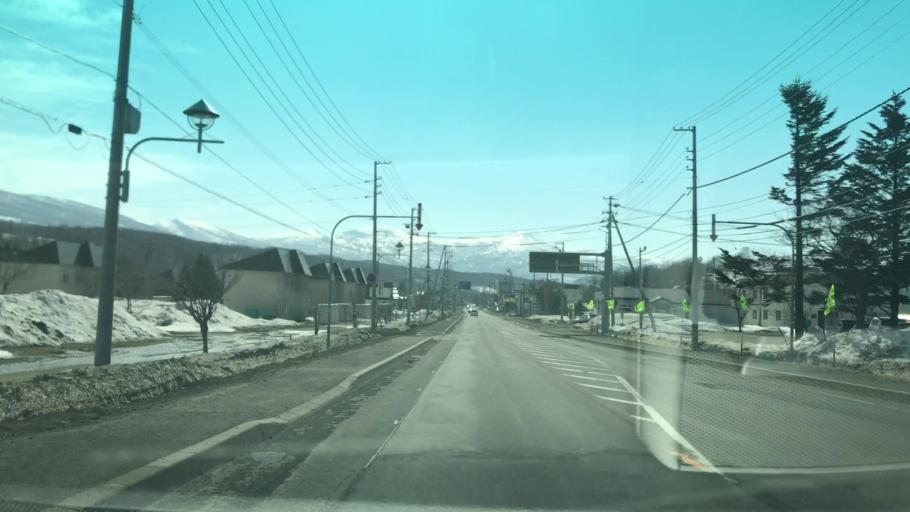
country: JP
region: Hokkaido
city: Iwanai
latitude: 42.9839
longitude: 140.6543
